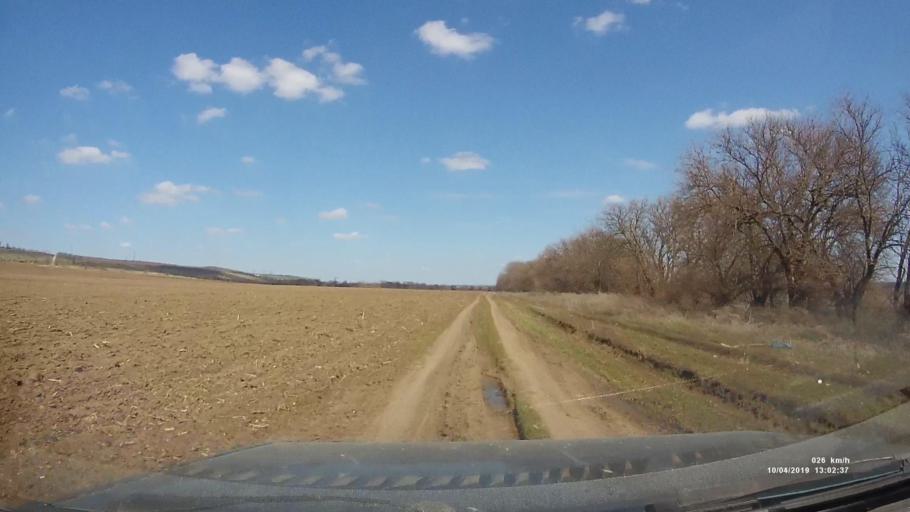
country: RU
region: Rostov
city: Masalovka
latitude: 48.3817
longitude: 40.2318
